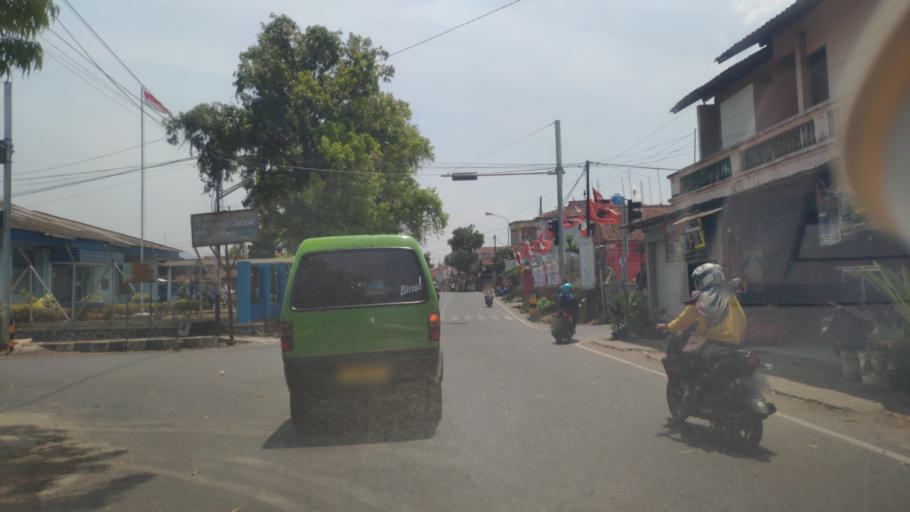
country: ID
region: Central Java
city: Wonosobo
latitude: -7.3911
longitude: 109.7059
